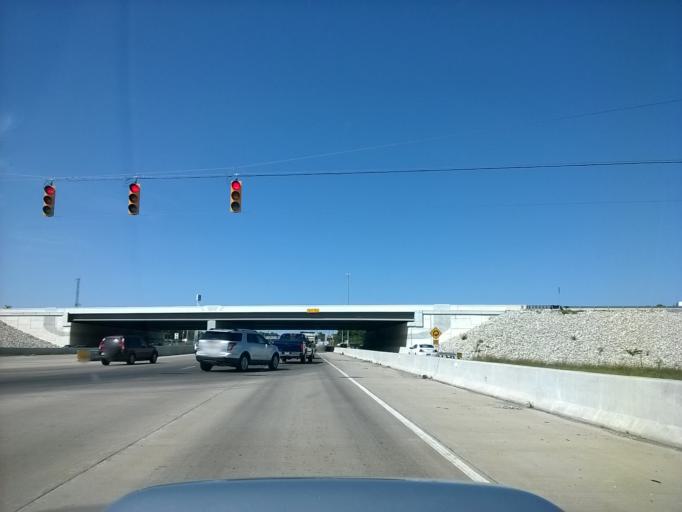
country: US
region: Indiana
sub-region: Marion County
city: Meridian Hills
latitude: 39.9201
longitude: -86.1121
